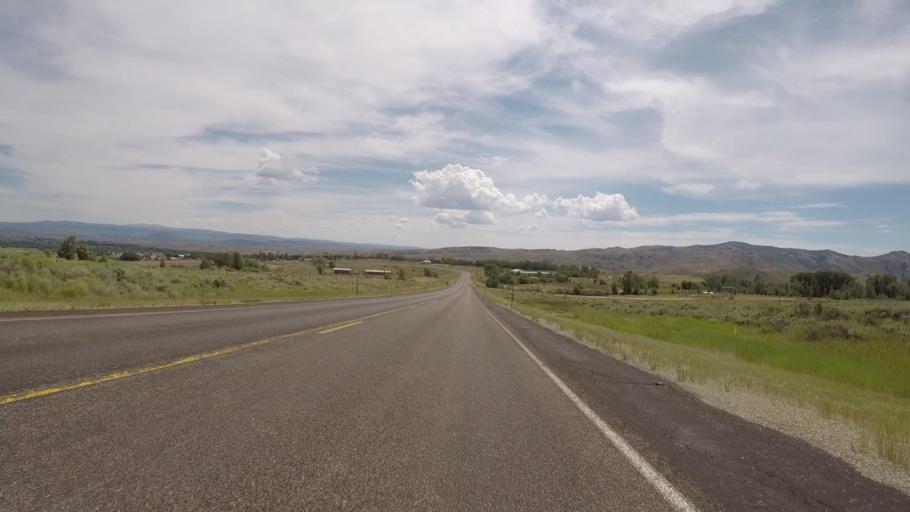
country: US
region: Wyoming
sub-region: Carbon County
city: Saratoga
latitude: 41.2056
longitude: -106.8120
